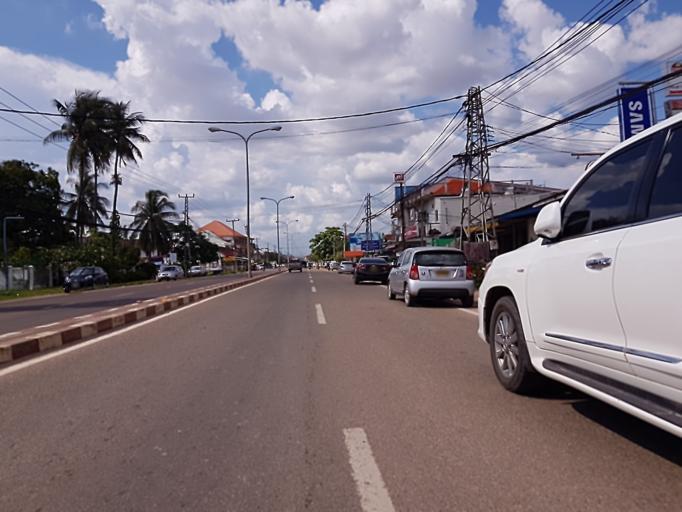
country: TH
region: Nong Khai
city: Si Chiang Mai
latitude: 17.9127
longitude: 102.6202
